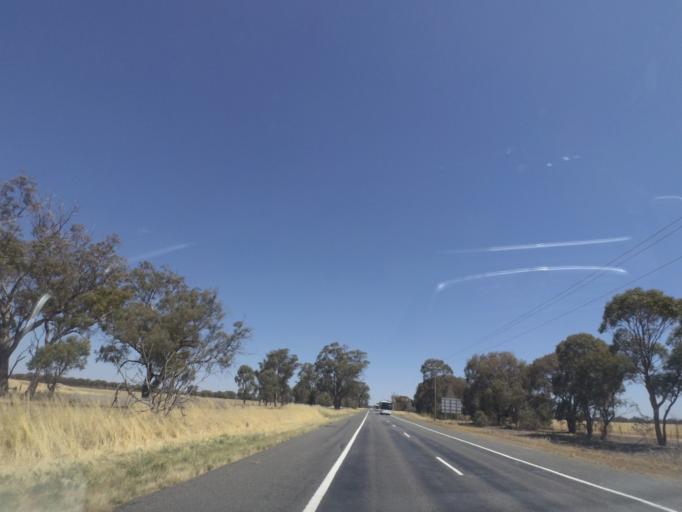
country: AU
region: Victoria
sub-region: Greater Shepparton
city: Shepparton
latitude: -36.2065
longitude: 145.4319
